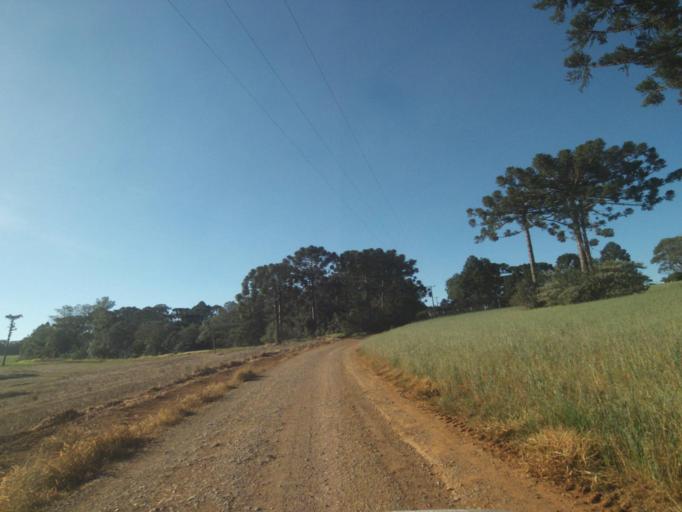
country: BR
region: Parana
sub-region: Tibagi
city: Tibagi
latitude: -24.5360
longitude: -50.4965
